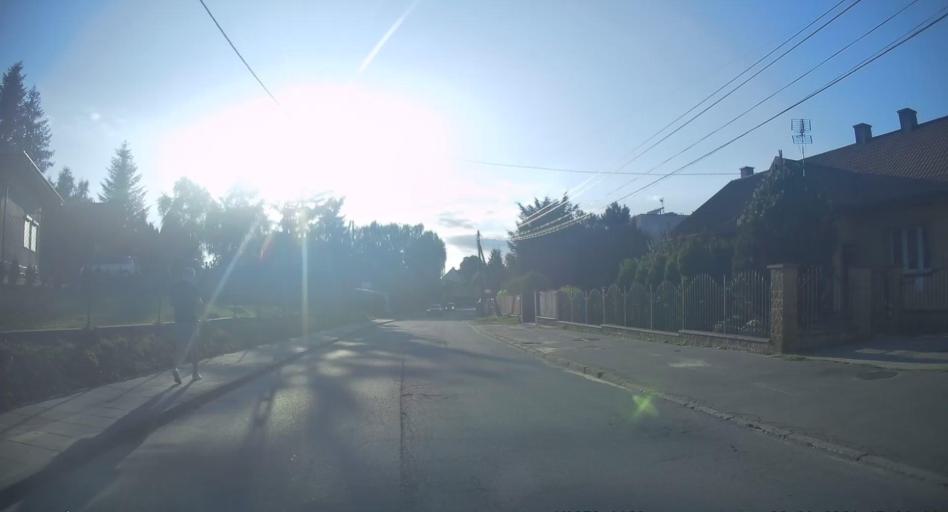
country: PL
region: Lesser Poland Voivodeship
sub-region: Powiat wielicki
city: Czarnochowice
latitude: 50.0174
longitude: 20.0457
